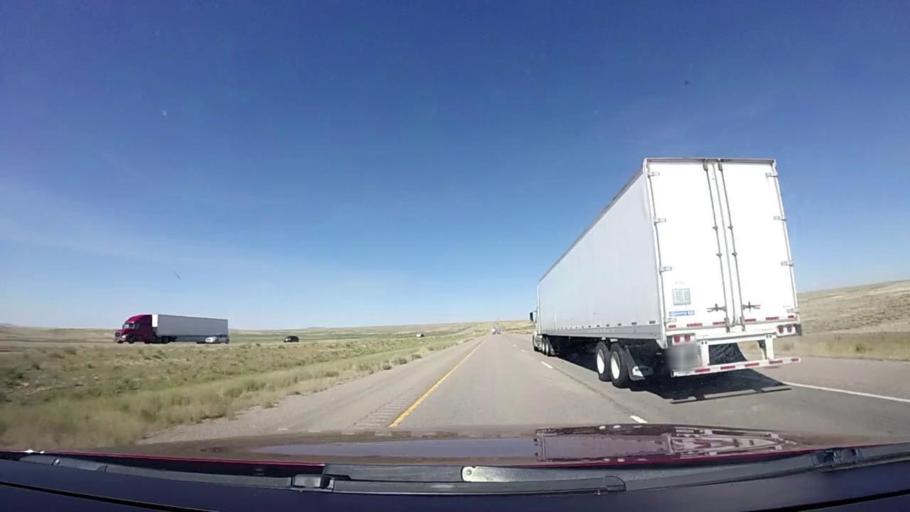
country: US
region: Wyoming
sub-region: Sweetwater County
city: Rock Springs
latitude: 41.6407
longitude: -108.4936
